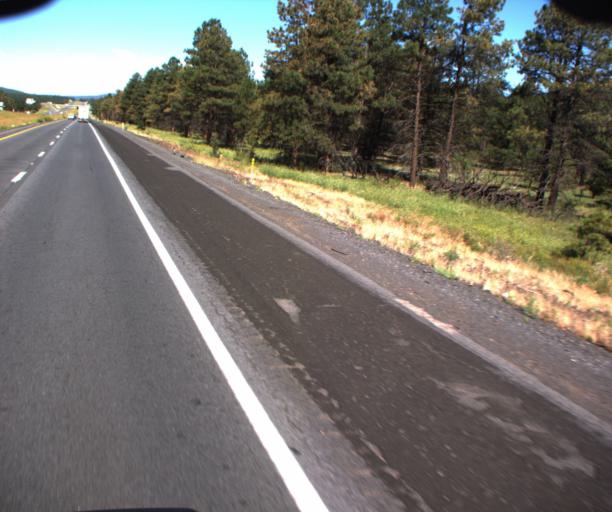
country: US
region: Arizona
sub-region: Coconino County
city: Williams
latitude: 35.2585
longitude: -112.1064
